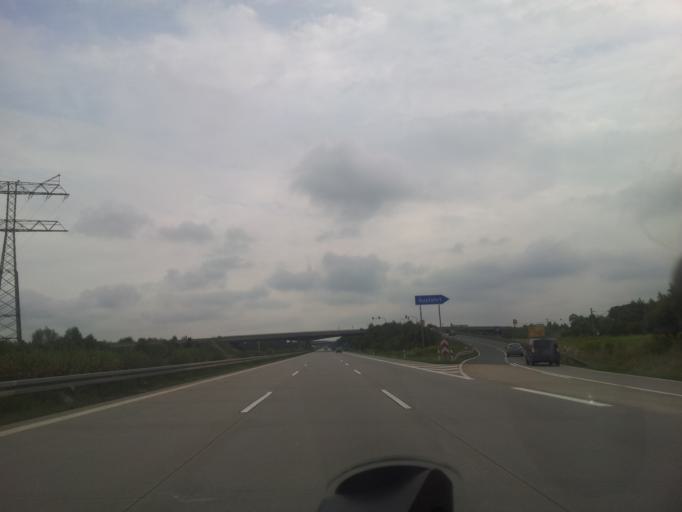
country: DE
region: Saxony
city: Zwochau
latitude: 51.4151
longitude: 12.3074
